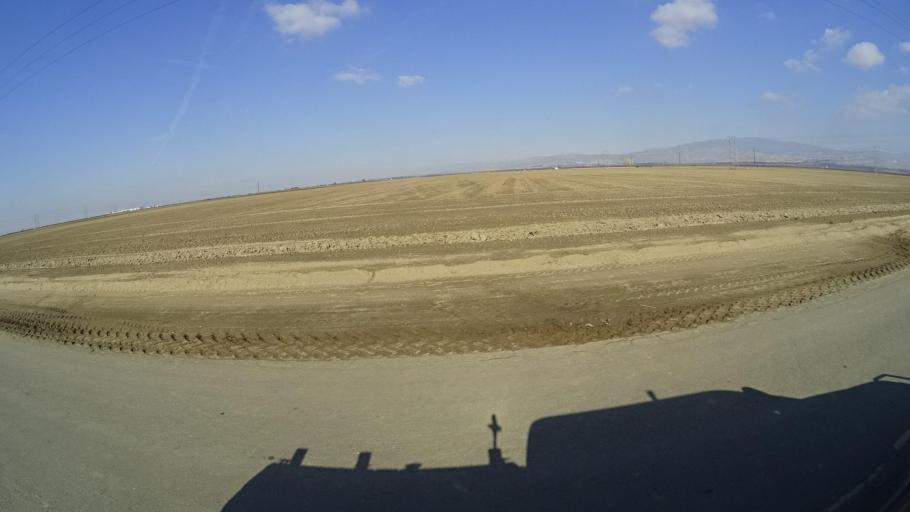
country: US
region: California
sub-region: Kern County
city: Arvin
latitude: 35.2384
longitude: -118.8087
